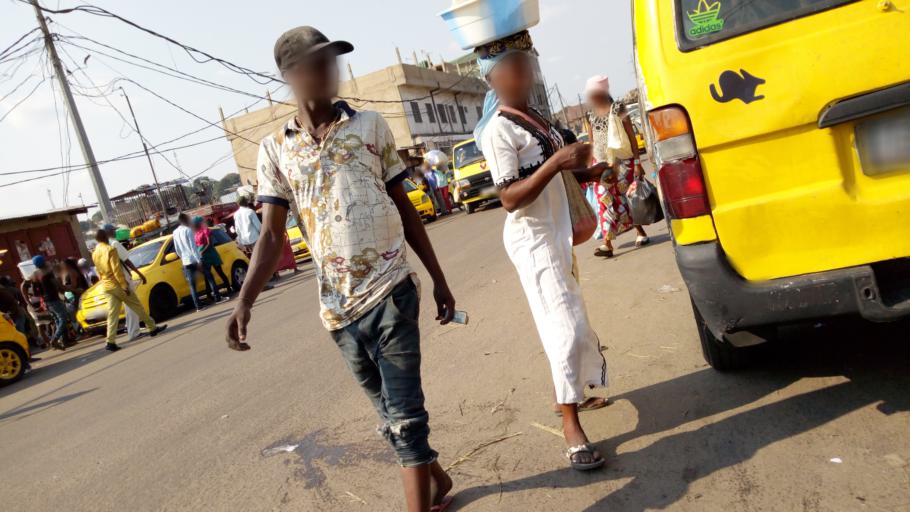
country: CD
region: Kinshasa
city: Kinshasa
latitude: -4.4485
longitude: 15.2487
